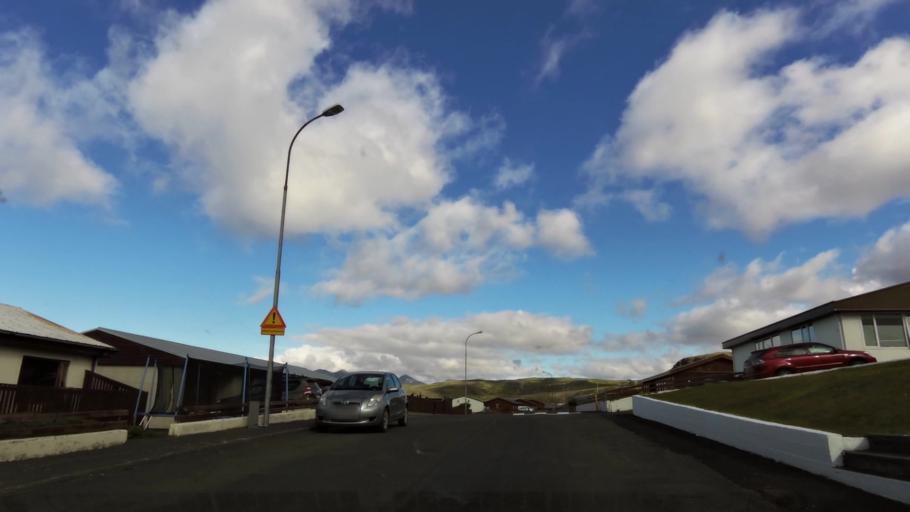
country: IS
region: West
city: Olafsvik
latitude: 64.8908
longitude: -23.7075
